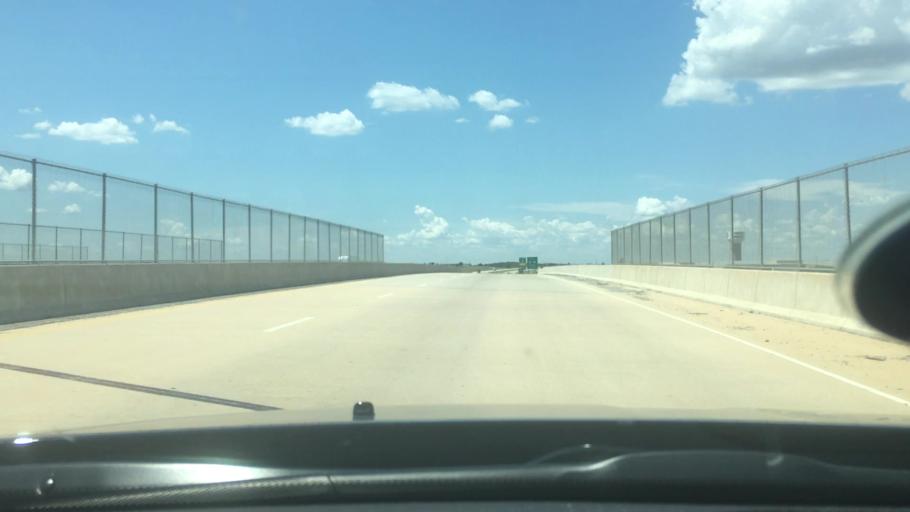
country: US
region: Oklahoma
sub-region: Bryan County
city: Durant
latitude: 33.9656
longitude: -96.3943
